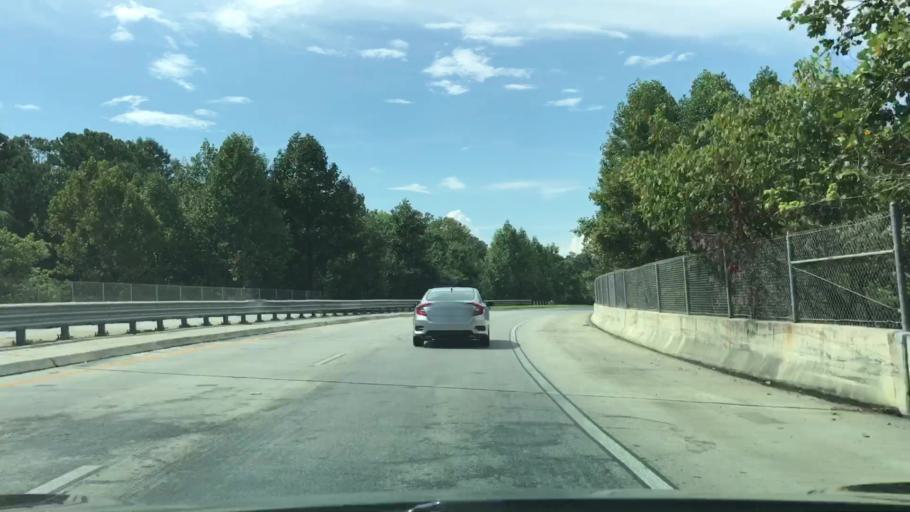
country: US
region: Georgia
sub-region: Gwinnett County
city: Snellville
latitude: 33.8958
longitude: -84.0670
